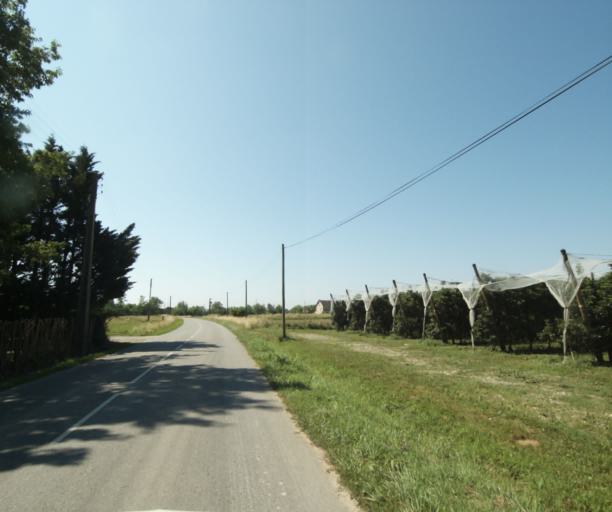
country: FR
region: Midi-Pyrenees
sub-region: Departement du Tarn-et-Garonne
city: Montbeton
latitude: 44.0457
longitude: 1.2926
